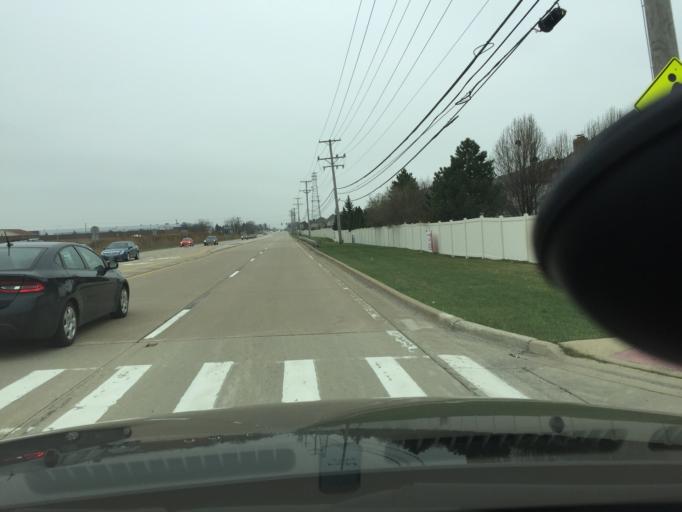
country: US
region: Illinois
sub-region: Cook County
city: Tinley Park
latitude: 41.5622
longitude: -87.8125
